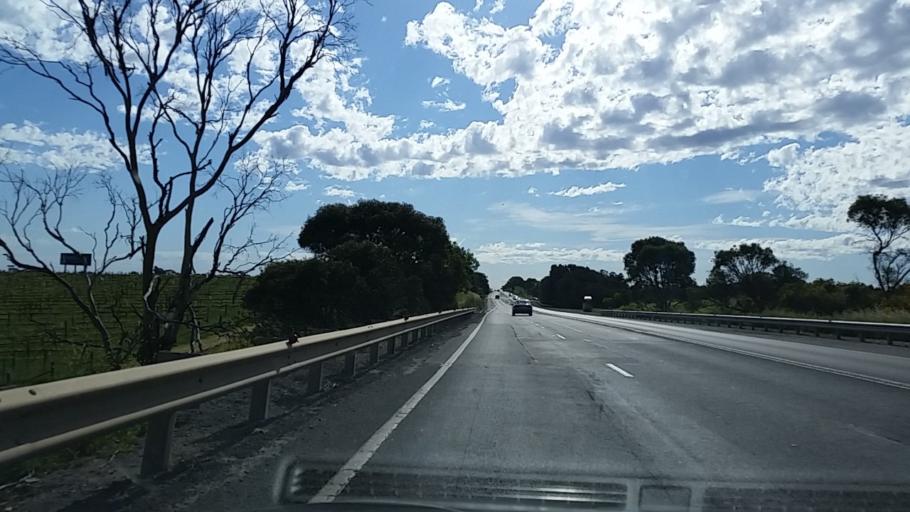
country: AU
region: South Australia
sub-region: Onkaparinga
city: Noarlunga
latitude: -35.1973
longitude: 138.5153
